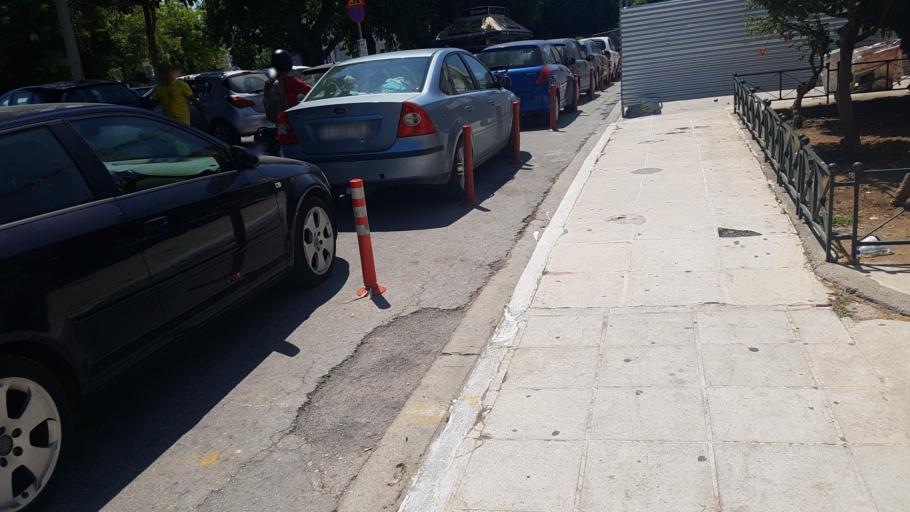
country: GR
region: Crete
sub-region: Nomos Chanias
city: Chania
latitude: 35.5149
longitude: 24.0207
